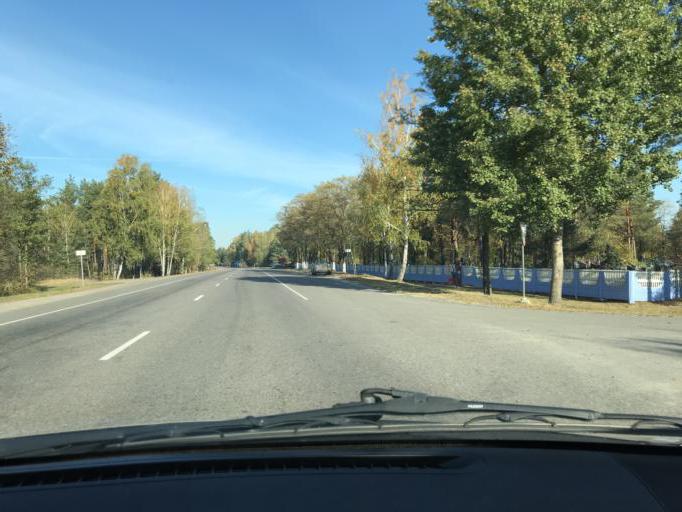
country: BY
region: Brest
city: Mikashevichy
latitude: 52.2353
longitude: 27.4487
